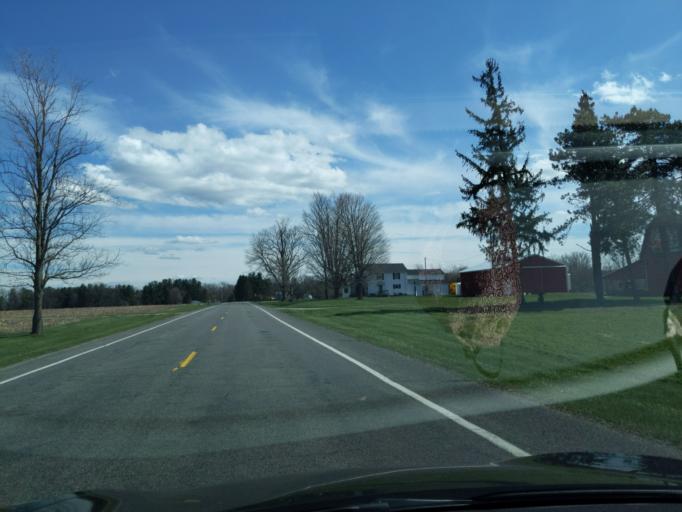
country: US
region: Michigan
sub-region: Ingham County
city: Mason
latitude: 42.5637
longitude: -84.4109
